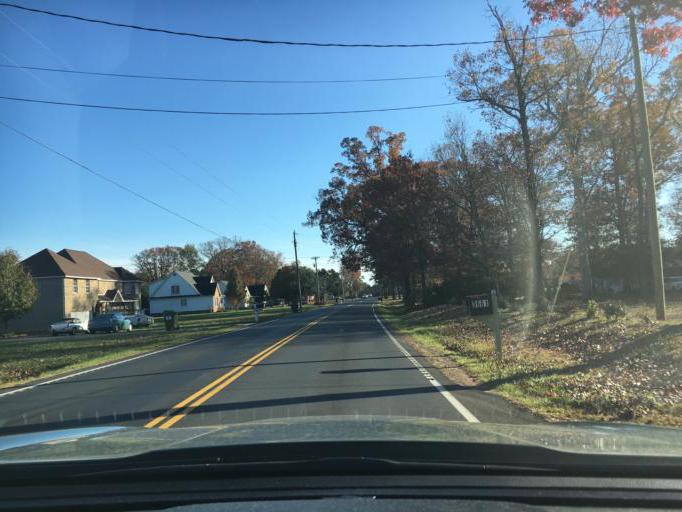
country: US
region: South Carolina
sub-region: Spartanburg County
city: Inman
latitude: 35.0116
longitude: -82.0752
